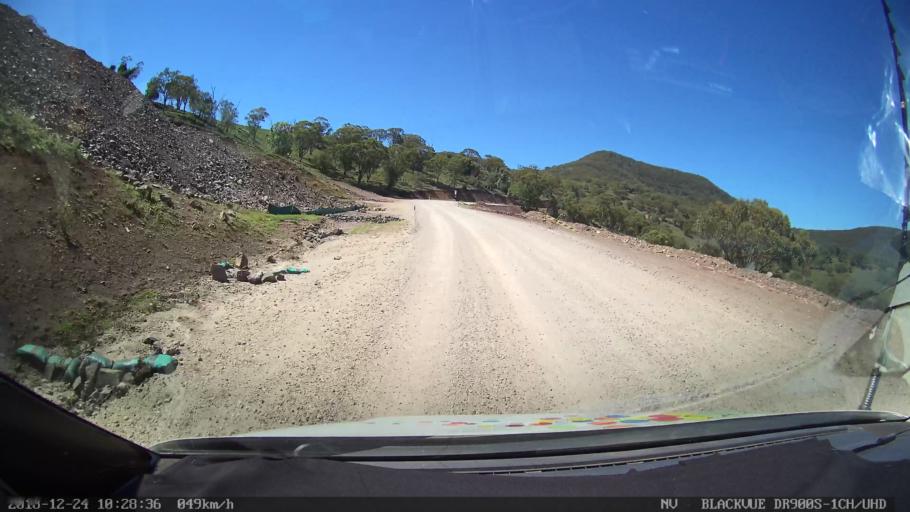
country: AU
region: New South Wales
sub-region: Liverpool Plains
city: Quirindi
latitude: -31.8269
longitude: 150.5314
